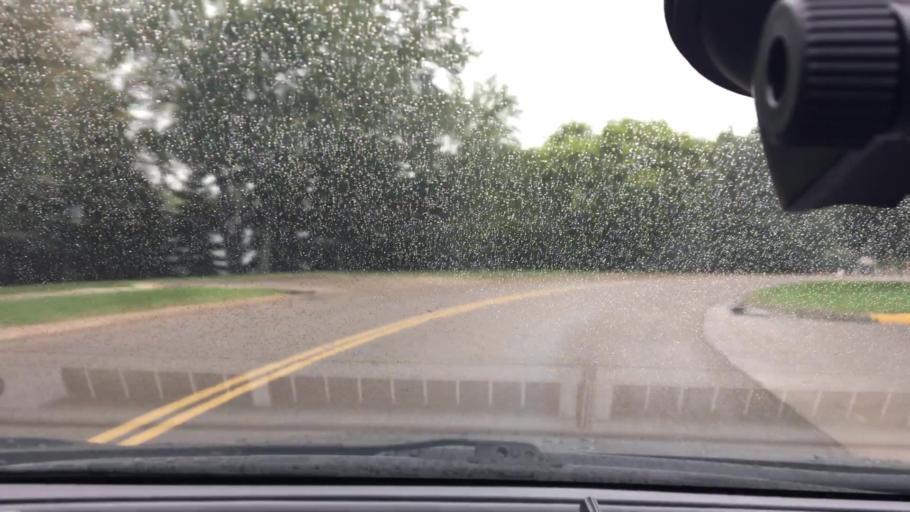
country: US
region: Minnesota
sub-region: Hennepin County
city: New Hope
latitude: 45.0066
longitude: -93.3982
